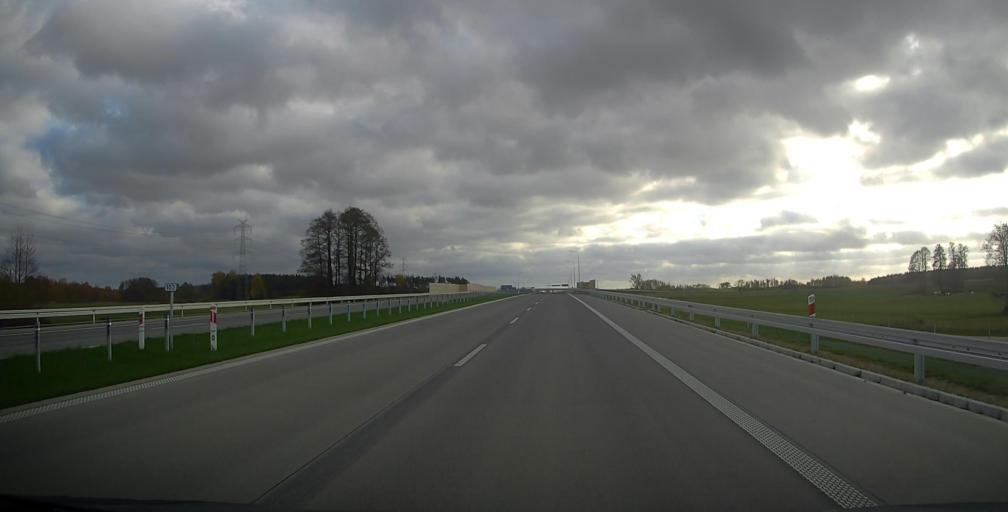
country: PL
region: Podlasie
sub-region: Powiat grajewski
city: Szczuczyn
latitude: 53.5996
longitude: 22.3260
